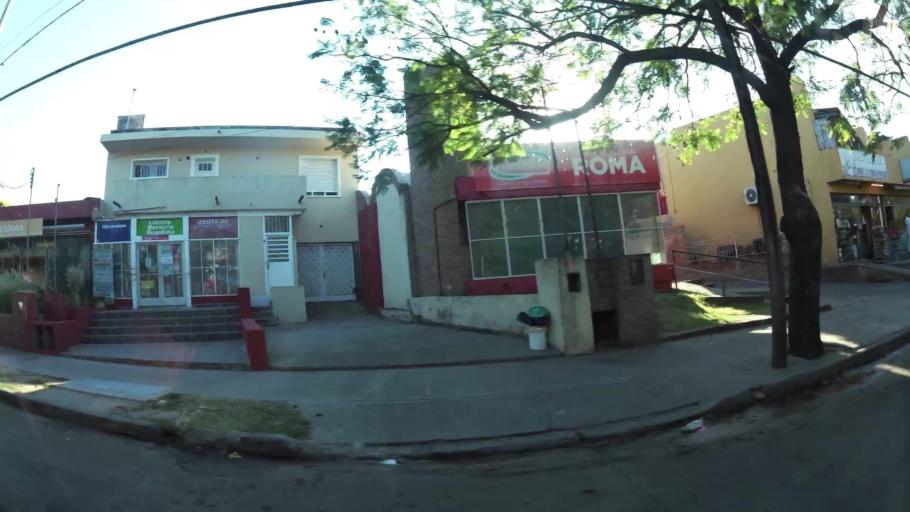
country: AR
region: Cordoba
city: Villa Allende
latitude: -31.3488
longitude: -64.2490
